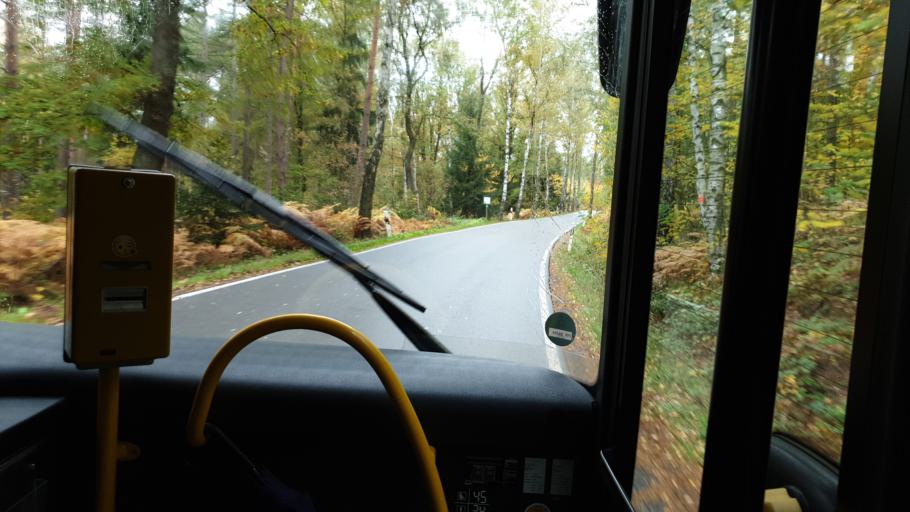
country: DE
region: Saxony
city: Kurort Gohrisch
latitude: 50.8901
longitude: 14.1027
